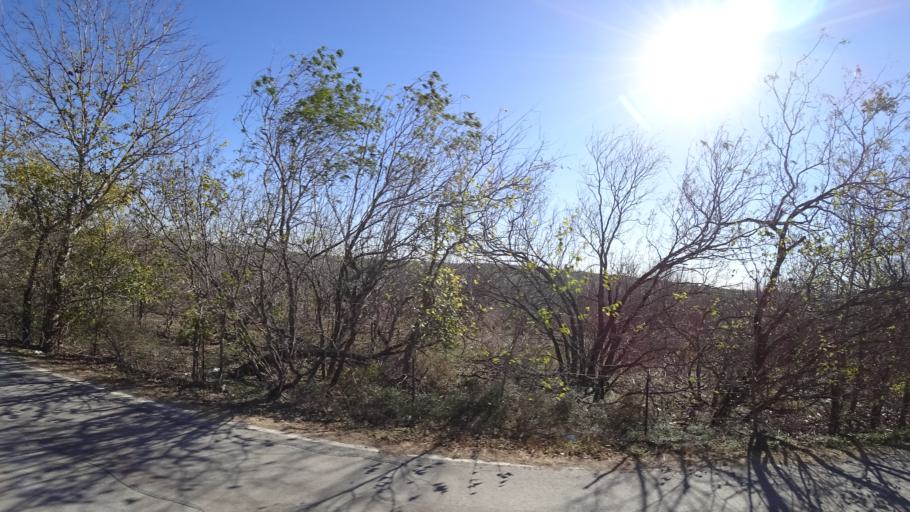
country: US
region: Texas
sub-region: Travis County
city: Onion Creek
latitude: 30.1148
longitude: -97.6721
